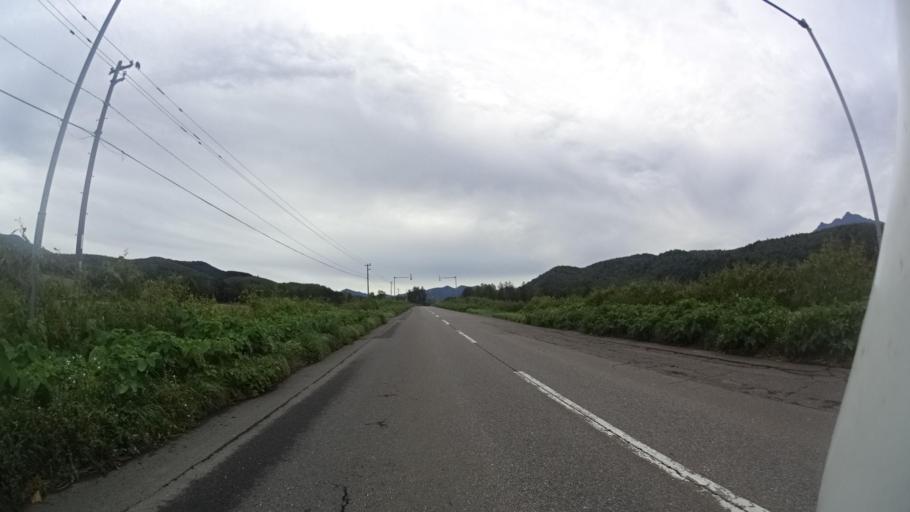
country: JP
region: Hokkaido
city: Shibetsu
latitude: 43.8568
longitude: 144.7655
